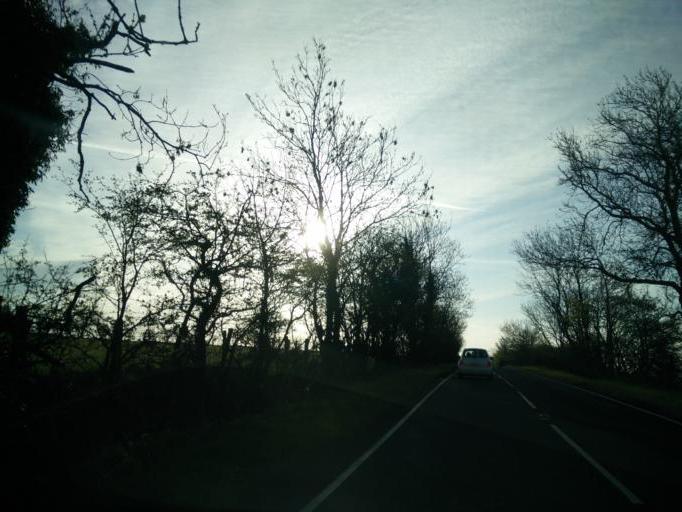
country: GB
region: England
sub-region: County Durham
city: Crook
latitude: 54.6756
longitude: -1.7158
